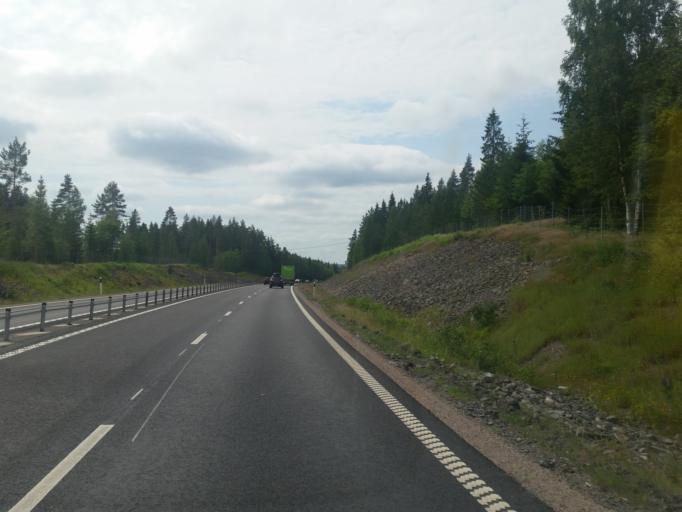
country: SE
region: Dalarna
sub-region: Borlange Kommun
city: Borlaenge
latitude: 60.4457
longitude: 15.3673
